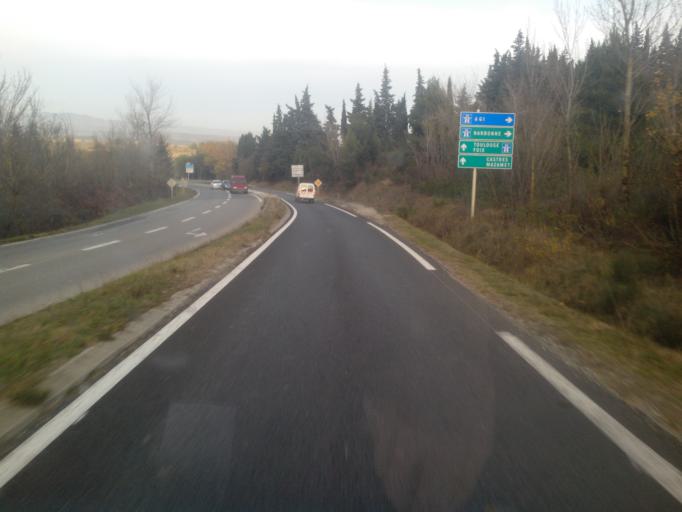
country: FR
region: Languedoc-Roussillon
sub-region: Departement de l'Aude
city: Palaja
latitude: 43.2044
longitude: 2.3872
